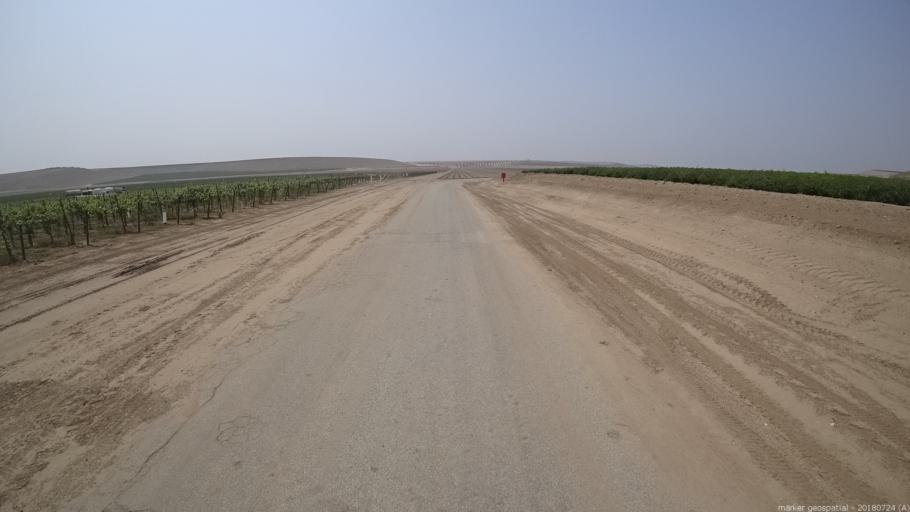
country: US
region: California
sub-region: Monterey County
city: King City
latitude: 36.1546
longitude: -121.0167
